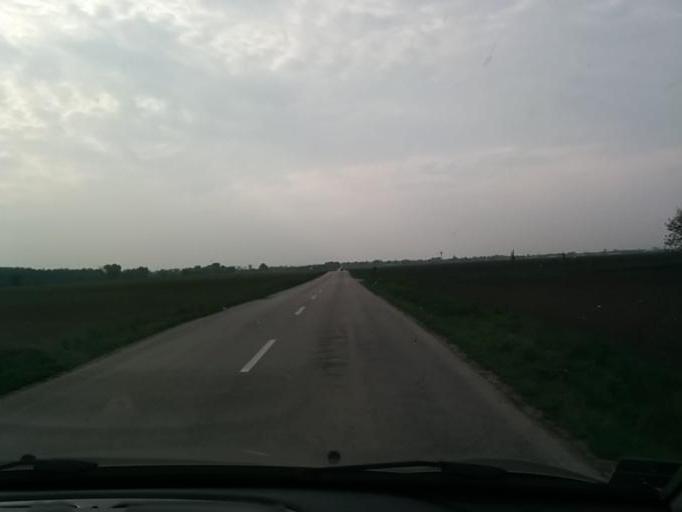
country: SK
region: Trnavsky
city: Sladkovicovo
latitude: 48.2189
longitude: 17.5928
